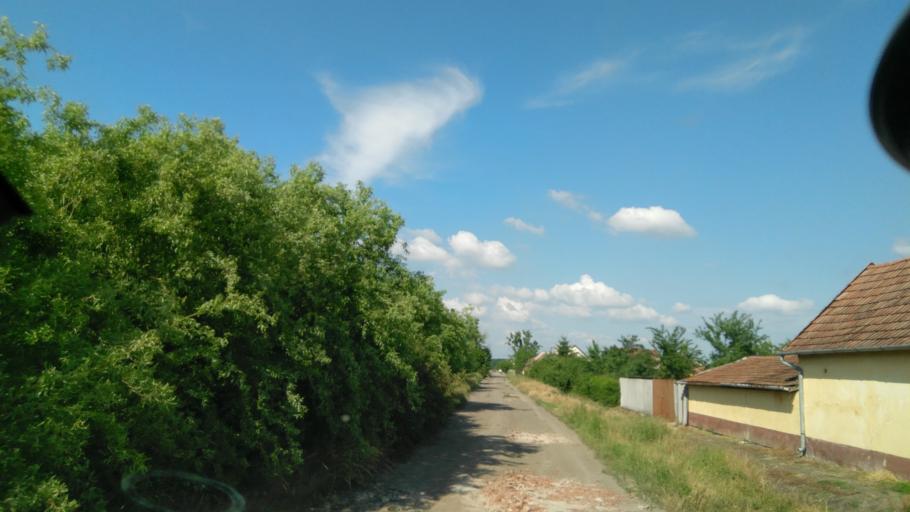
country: HU
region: Bekes
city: Bekes
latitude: 46.7047
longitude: 21.1756
